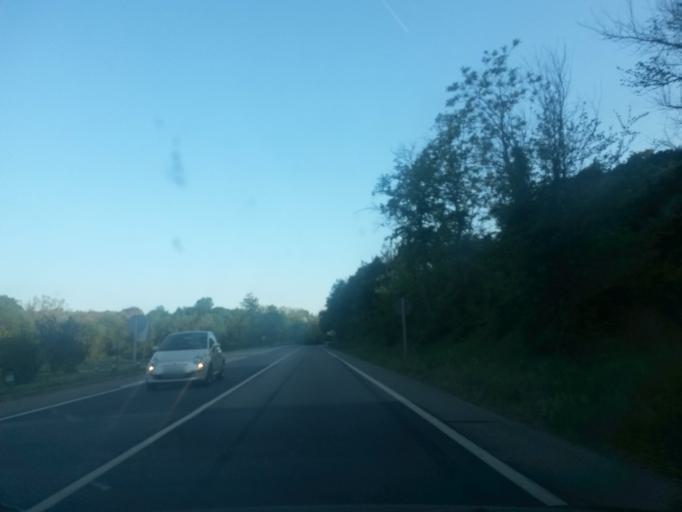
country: ES
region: Catalonia
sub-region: Provincia de Girona
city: Porqueres
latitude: 42.1651
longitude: 2.7448
